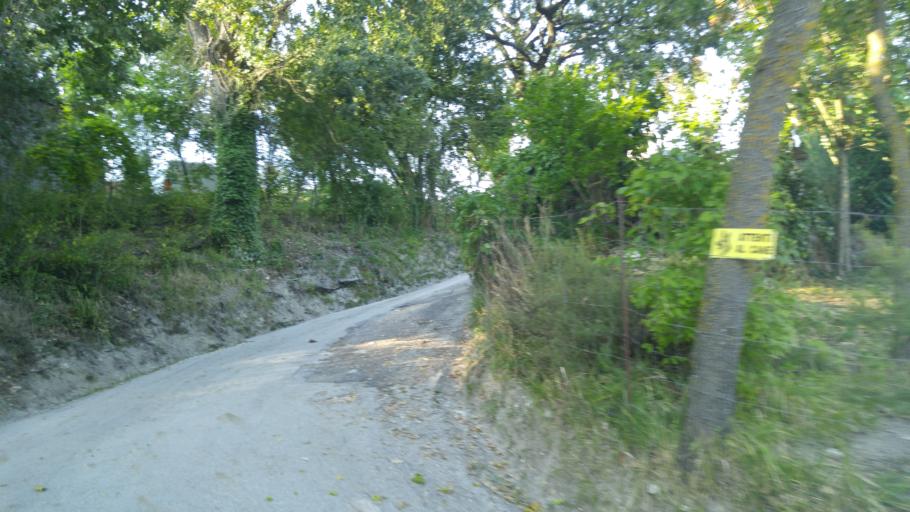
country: IT
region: The Marches
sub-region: Provincia di Pesaro e Urbino
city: Acqualagna
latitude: 43.6269
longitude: 12.6687
